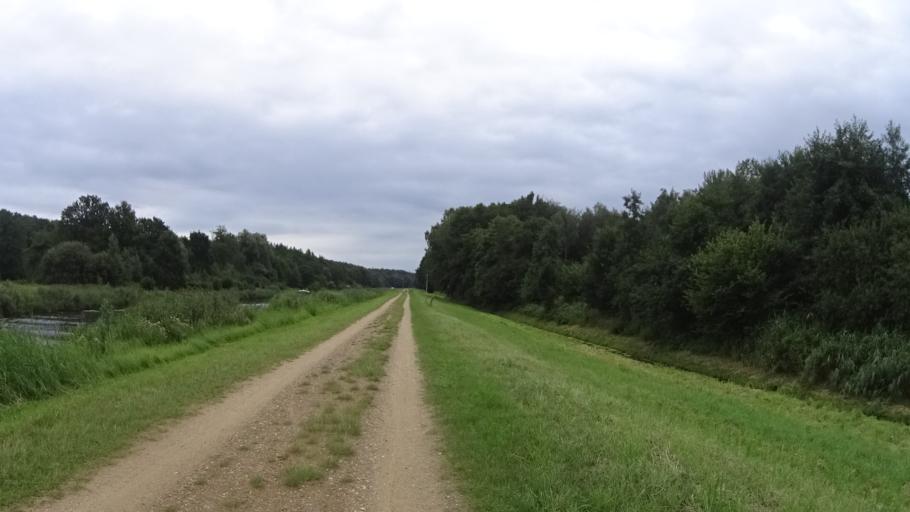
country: DE
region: Schleswig-Holstein
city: Panten
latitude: 53.6576
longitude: 10.6410
